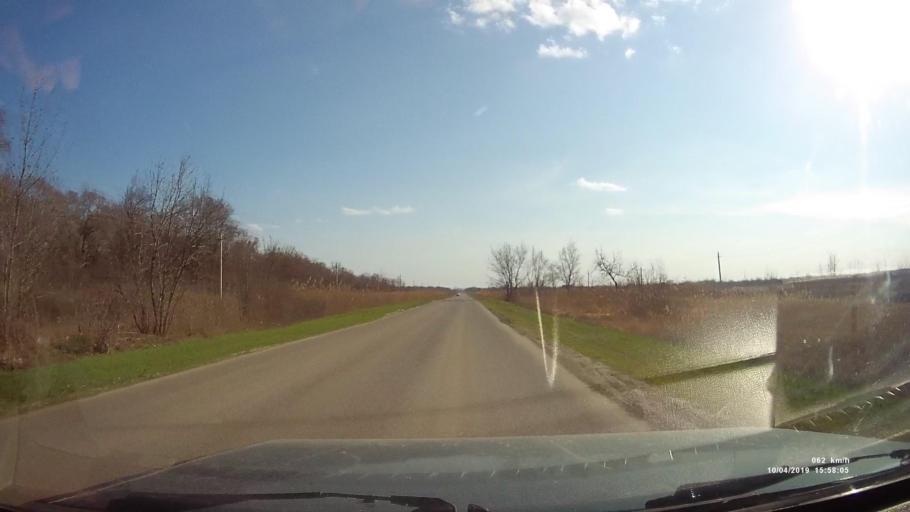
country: RU
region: Rostov
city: Masalovka
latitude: 48.4058
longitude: 40.2735
